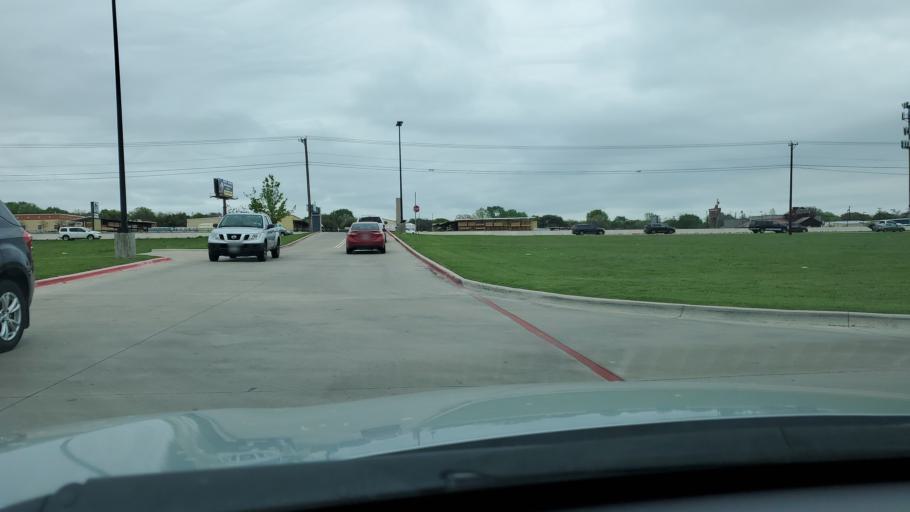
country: US
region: Texas
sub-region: Bell County
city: Harker Heights
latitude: 31.0721
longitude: -97.6798
